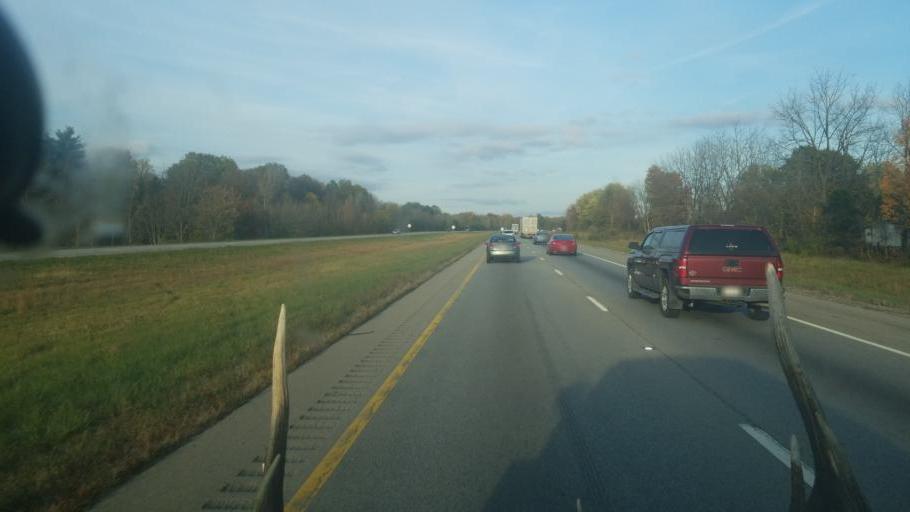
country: US
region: Ohio
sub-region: Franklin County
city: Reynoldsburg
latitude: 39.9462
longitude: -82.7563
